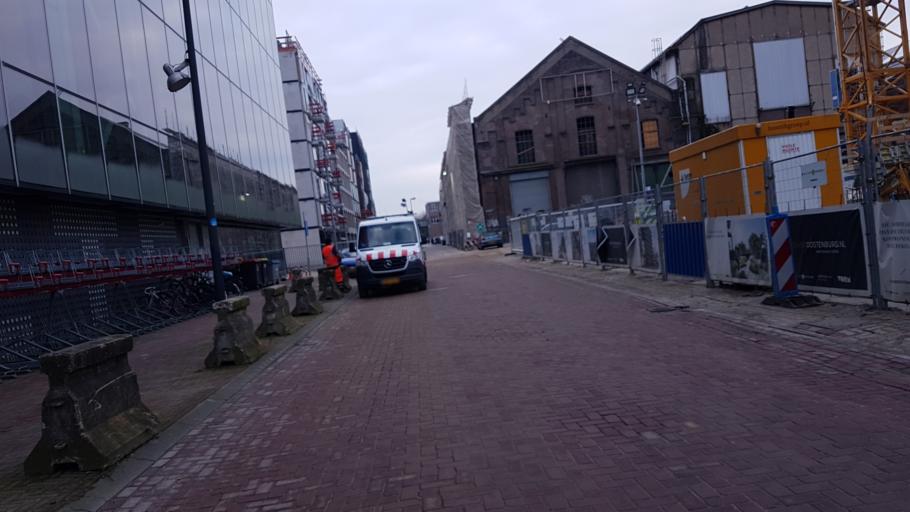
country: NL
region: North Holland
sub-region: Gemeente Amsterdam
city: Amsterdam
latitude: 52.3718
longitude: 4.9276
